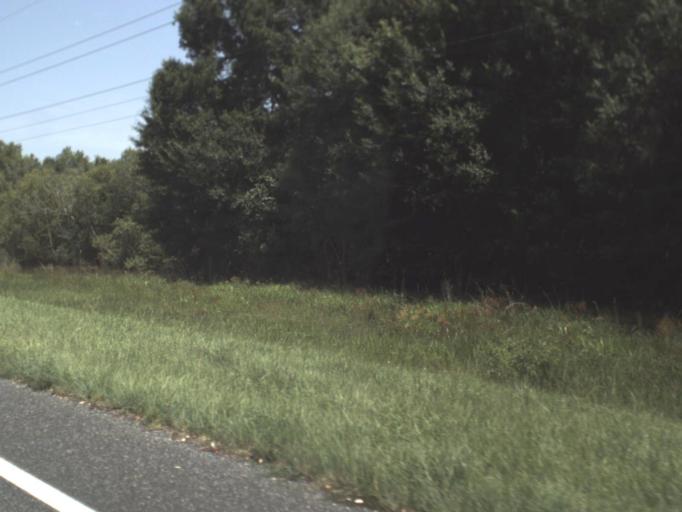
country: US
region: Florida
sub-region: Dixie County
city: Cross City
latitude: 29.6681
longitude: -83.2203
